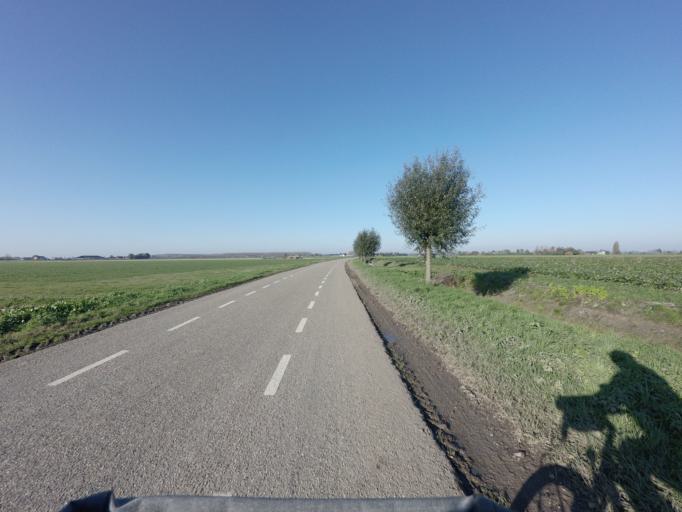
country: NL
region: North Brabant
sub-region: Gemeente Waalwijk
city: Waalwijk
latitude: 51.7452
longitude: 5.0611
